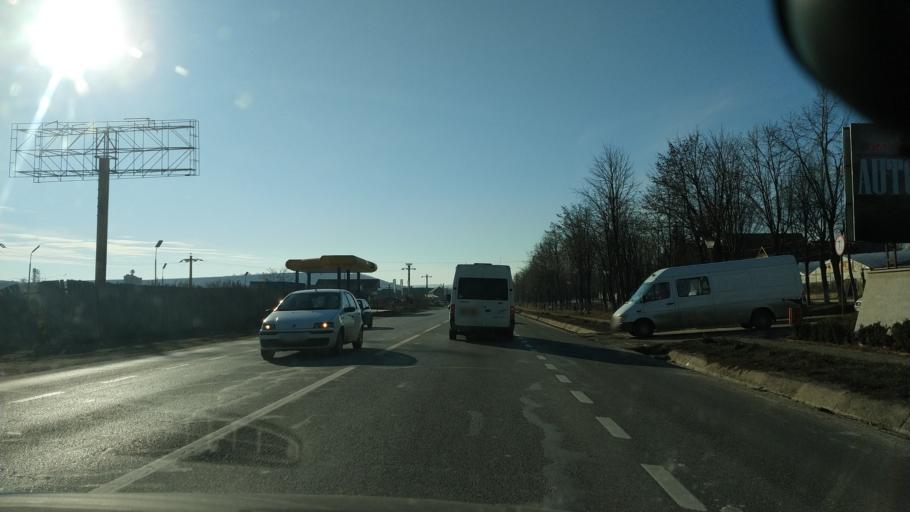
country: RO
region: Iasi
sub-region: Comuna Ion Neculce
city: Razboieni
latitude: 47.2149
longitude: 27.0280
